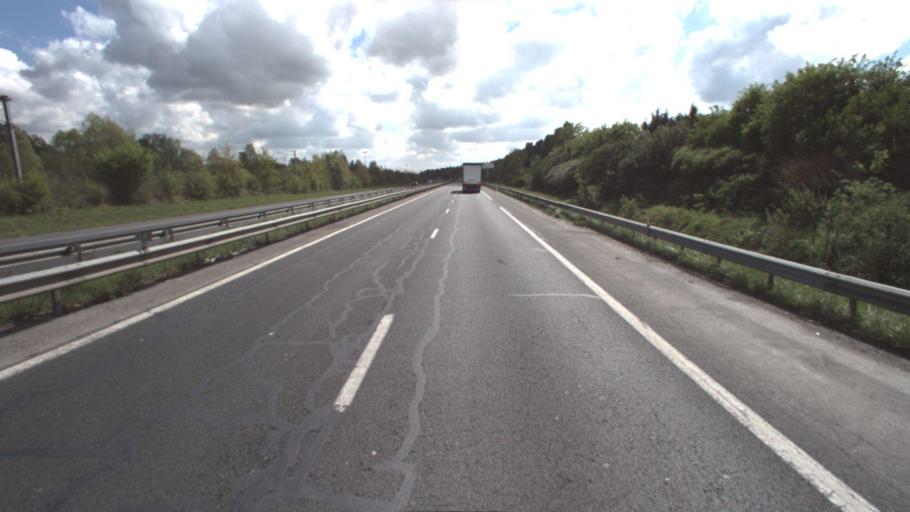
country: FR
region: Ile-de-France
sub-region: Departement de Seine-et-Marne
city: Tournan-en-Brie
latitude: 48.7304
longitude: 2.7966
